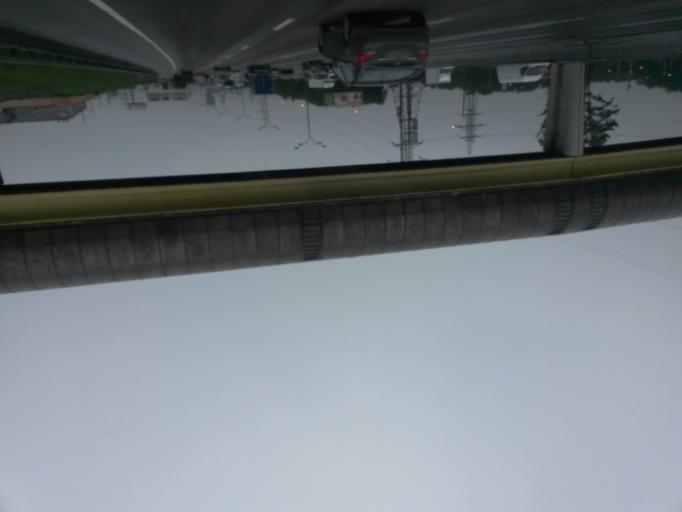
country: RU
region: Moscow
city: Yasenevo
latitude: 55.5993
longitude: 37.5063
